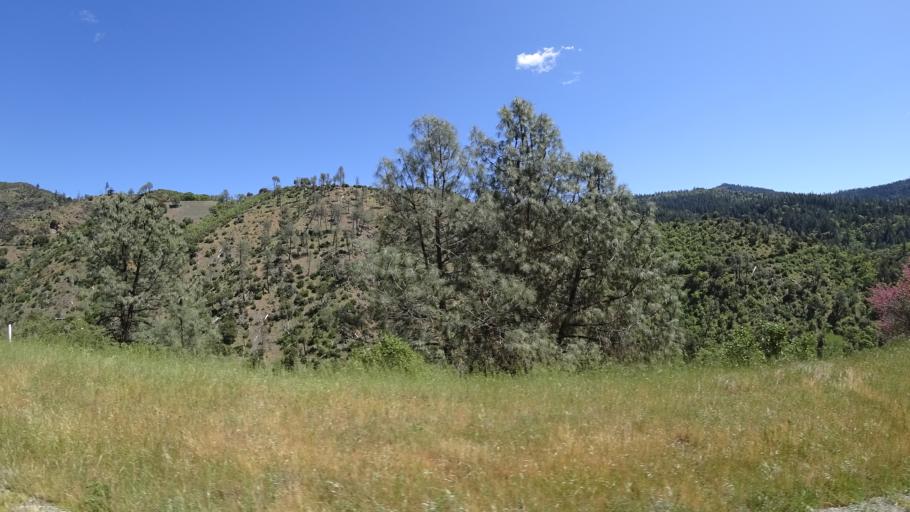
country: US
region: California
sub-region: Trinity County
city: Weaverville
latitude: 40.7379
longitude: -123.0069
